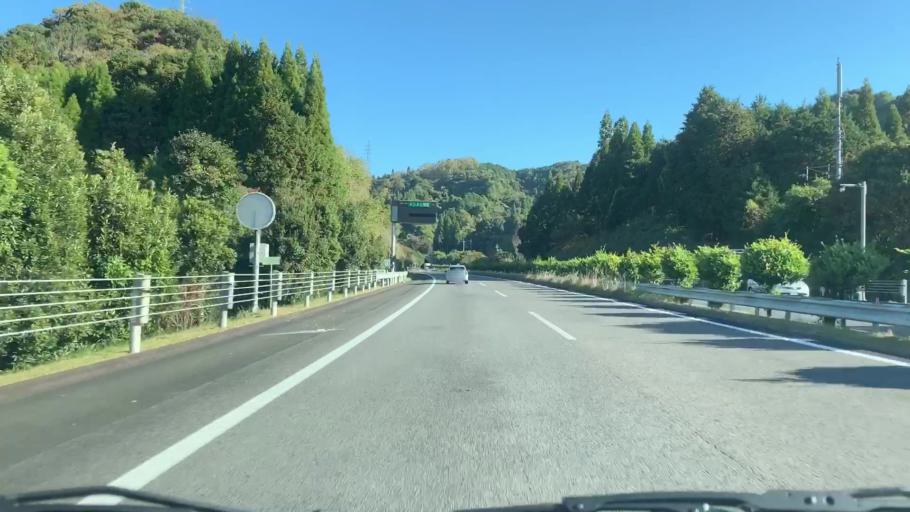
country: JP
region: Saga Prefecture
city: Takeocho-takeo
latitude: 33.2370
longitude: 130.0625
